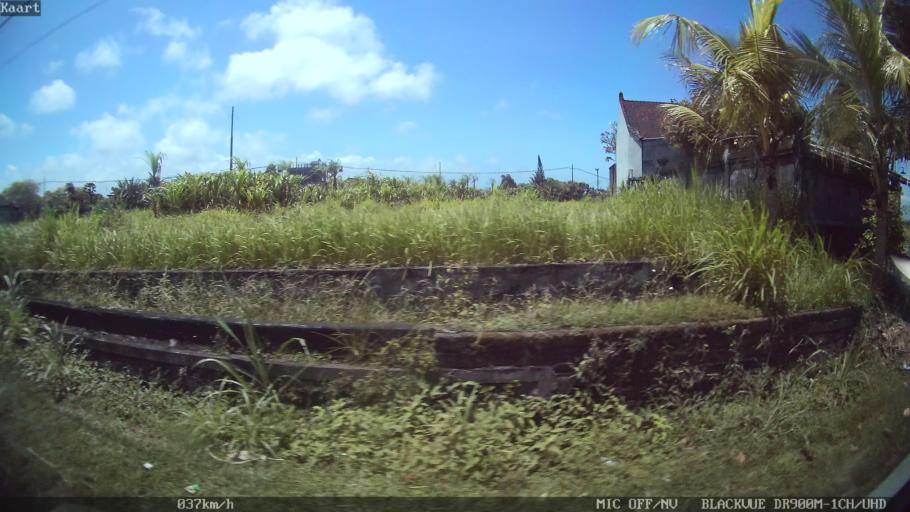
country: ID
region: Bali
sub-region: Kabupaten Gianyar
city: Ubud
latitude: -8.5640
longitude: 115.3198
